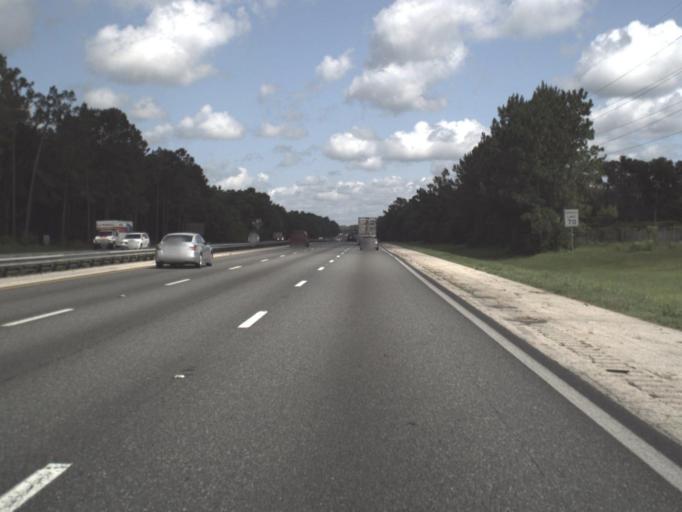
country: US
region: Florida
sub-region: Alachua County
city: Gainesville
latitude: 29.6257
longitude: -82.3918
